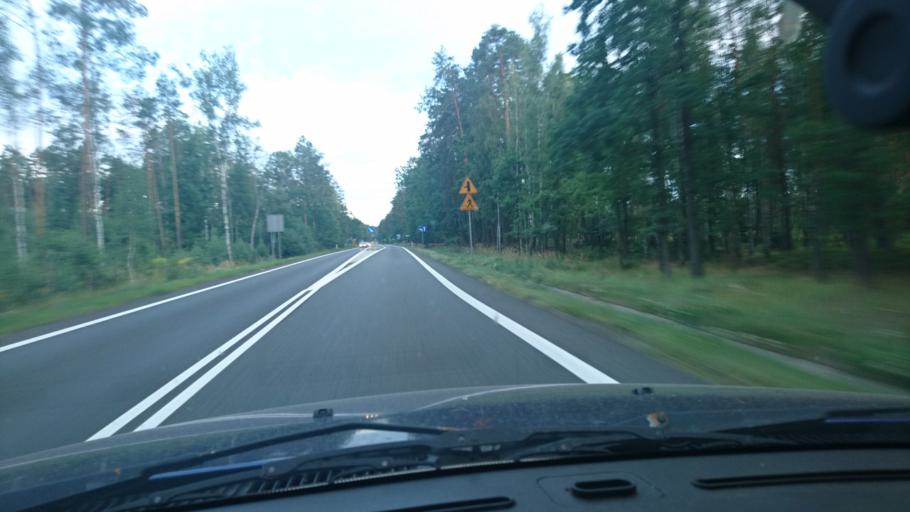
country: PL
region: Silesian Voivodeship
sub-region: Powiat lubliniecki
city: Lubliniec
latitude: 50.6075
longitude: 18.6966
